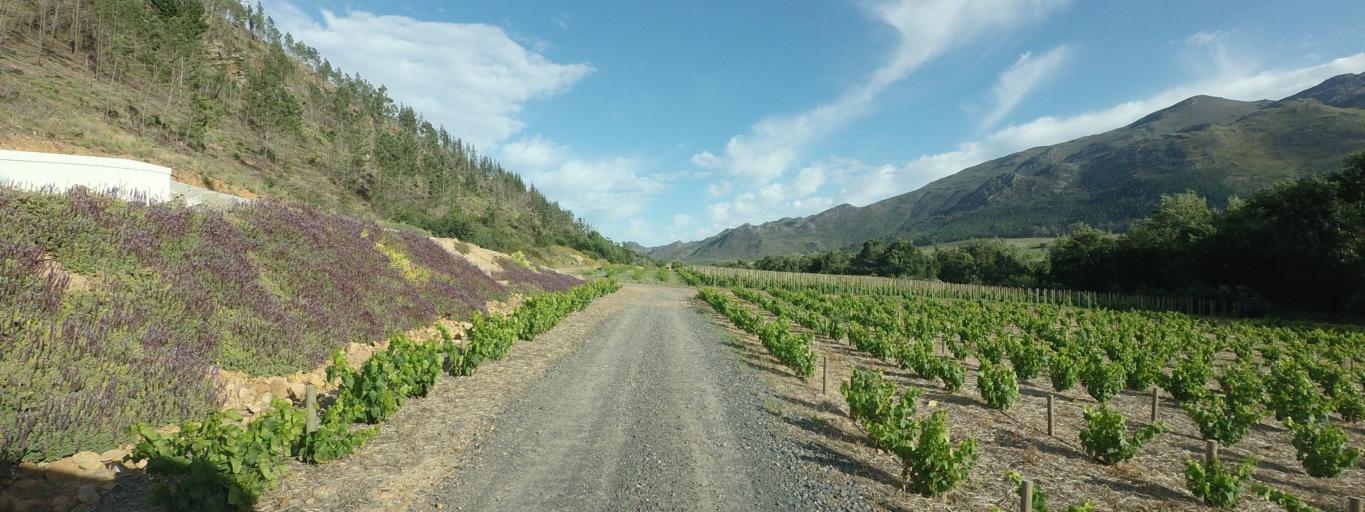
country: ZA
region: Western Cape
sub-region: Cape Winelands District Municipality
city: Paarl
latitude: -33.8982
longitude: 19.0909
